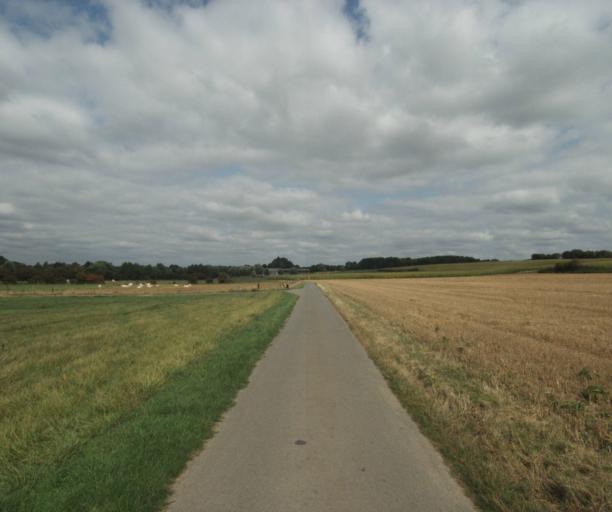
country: FR
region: Nord-Pas-de-Calais
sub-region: Departement du Nord
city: Anstaing
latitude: 50.5889
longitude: 3.1922
